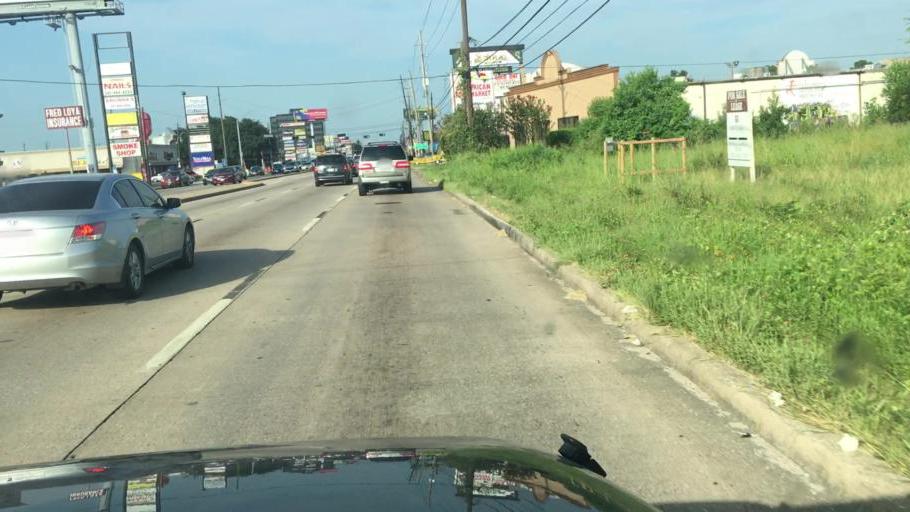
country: US
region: Texas
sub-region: Harris County
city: Spring
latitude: 30.0163
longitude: -95.4455
